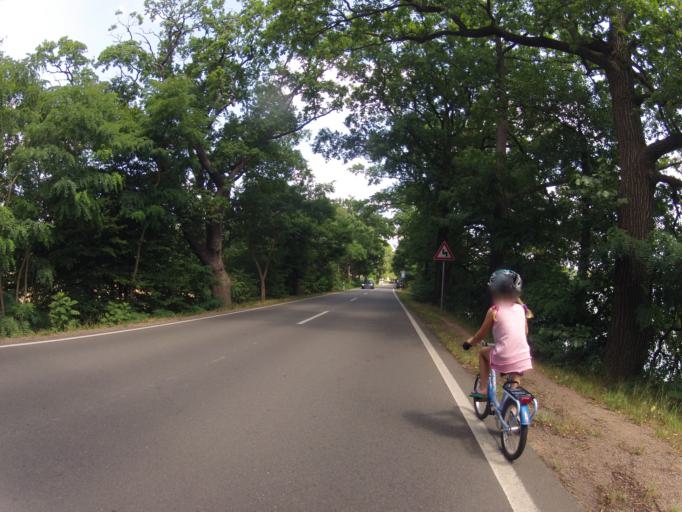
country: DE
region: Saxony
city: Schildau
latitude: 51.4713
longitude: 12.9444
